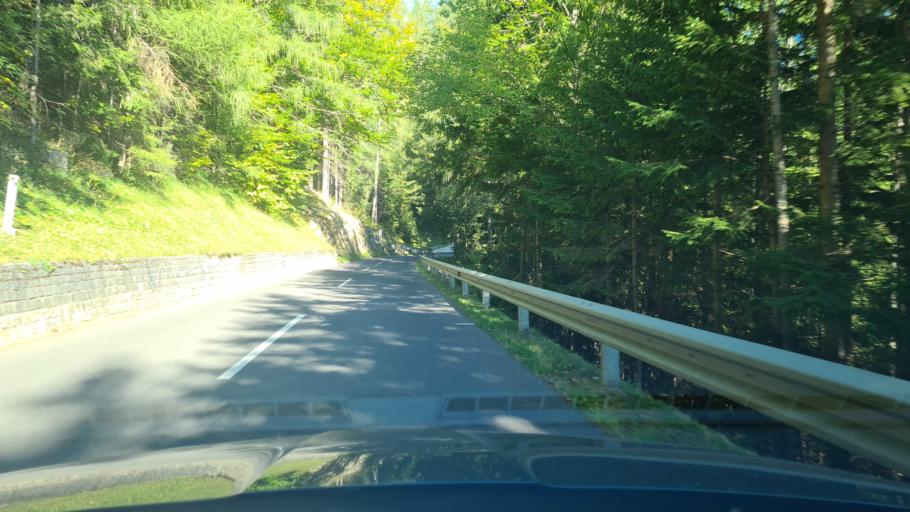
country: AT
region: Styria
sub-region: Politischer Bezirk Weiz
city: Passail
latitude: 47.3311
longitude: 15.4749
